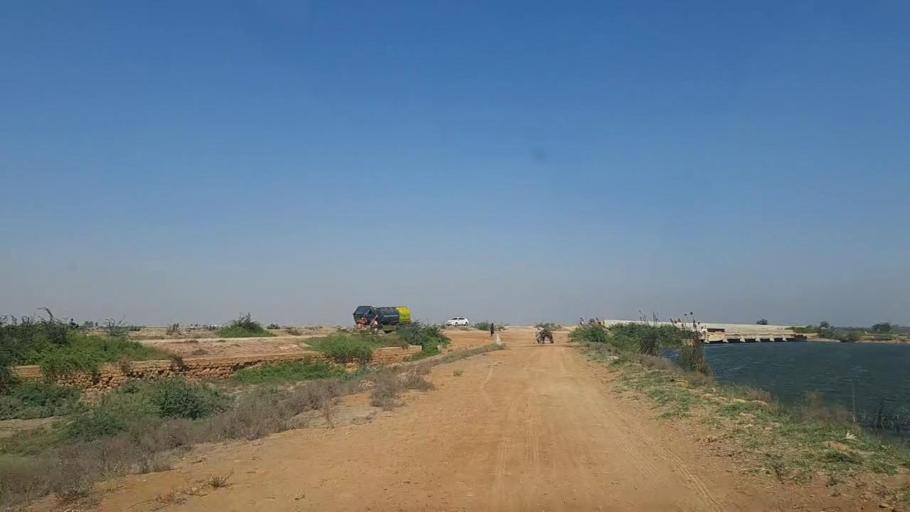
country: PK
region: Sindh
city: Thatta
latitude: 24.8248
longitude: 67.9907
